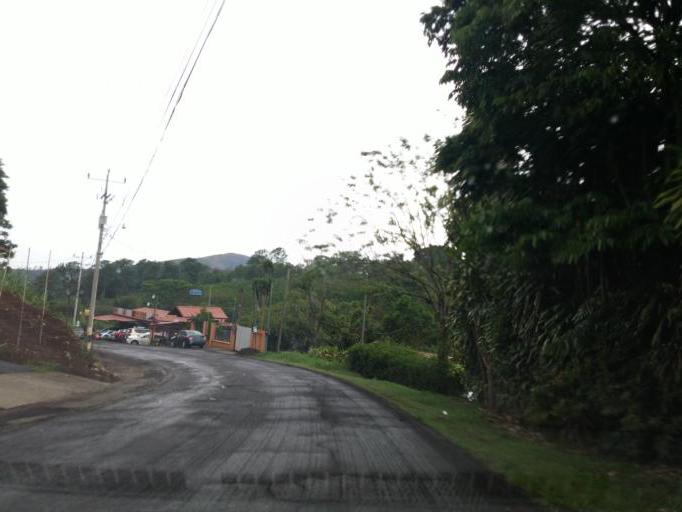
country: CR
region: Alajuela
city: Naranjo
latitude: 10.0877
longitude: -84.3537
